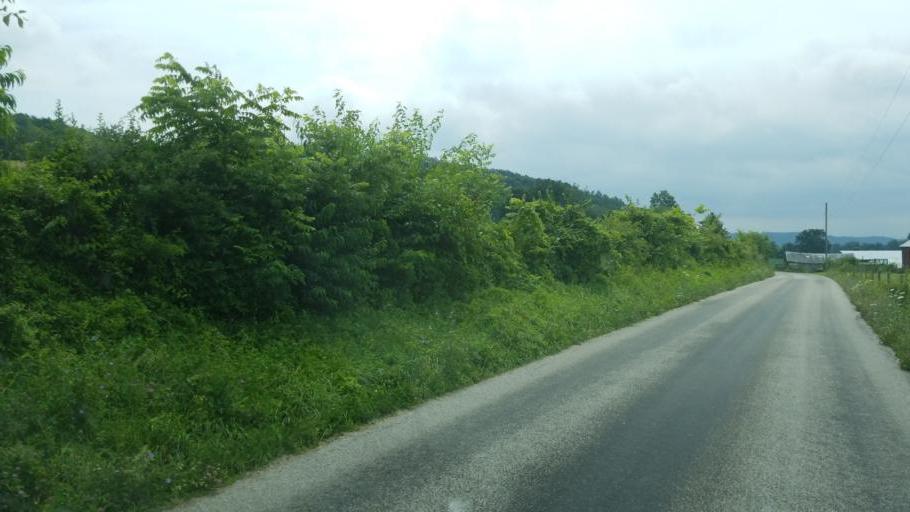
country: US
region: Ohio
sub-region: Licking County
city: Utica
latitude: 40.1726
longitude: -82.4314
